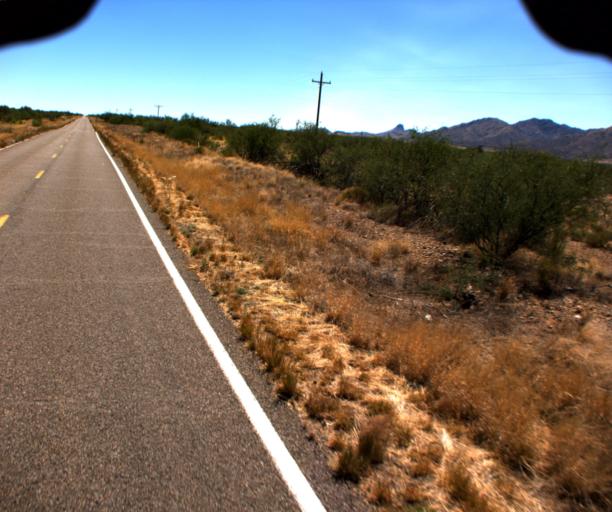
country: US
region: Arizona
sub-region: Pima County
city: Three Points
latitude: 31.7799
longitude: -111.4615
